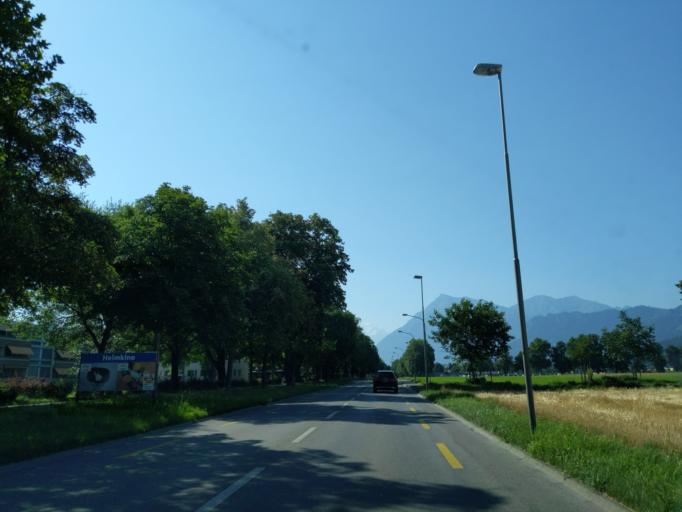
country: CH
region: Bern
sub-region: Thun District
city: Thun
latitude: 46.7513
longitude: 7.6093
